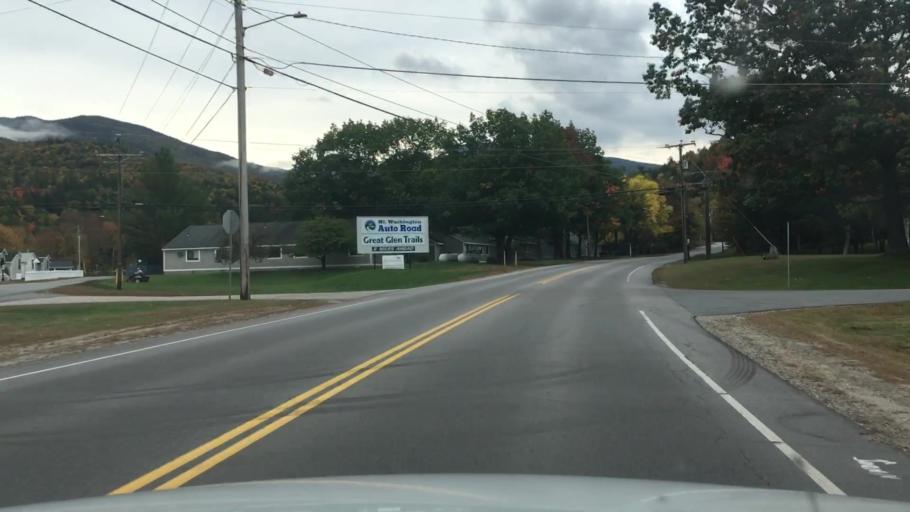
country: US
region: New Hampshire
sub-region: Coos County
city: Gorham
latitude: 44.3845
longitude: -71.1726
